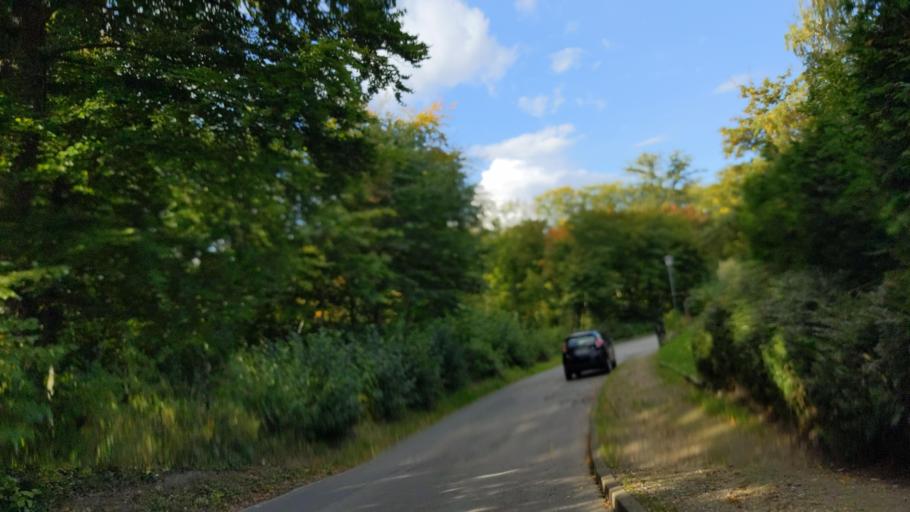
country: DE
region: Schleswig-Holstein
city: Scharbeutz
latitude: 54.0254
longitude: 10.7371
